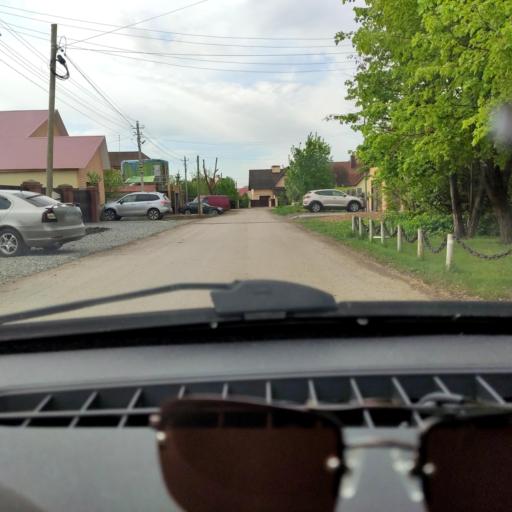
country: RU
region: Bashkortostan
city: Ufa
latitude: 54.6097
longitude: 55.9341
